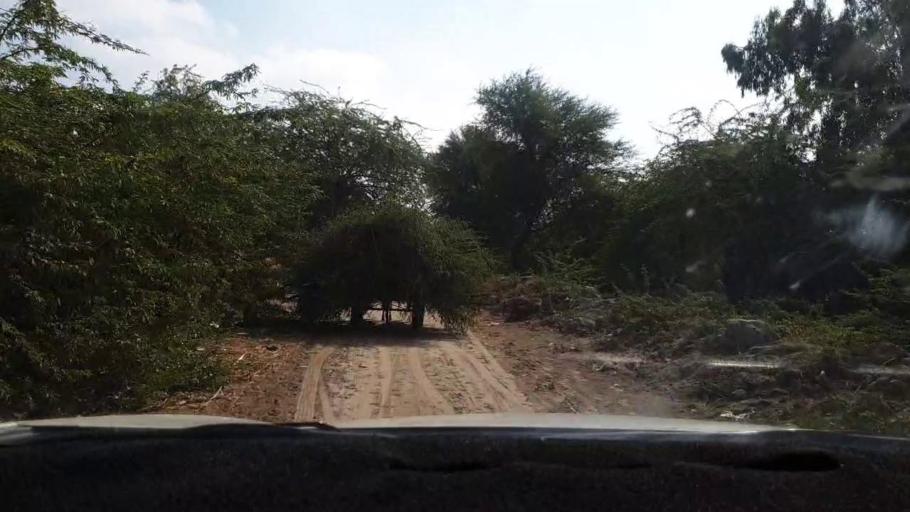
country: PK
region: Sindh
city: Berani
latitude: 25.7599
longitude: 68.9922
